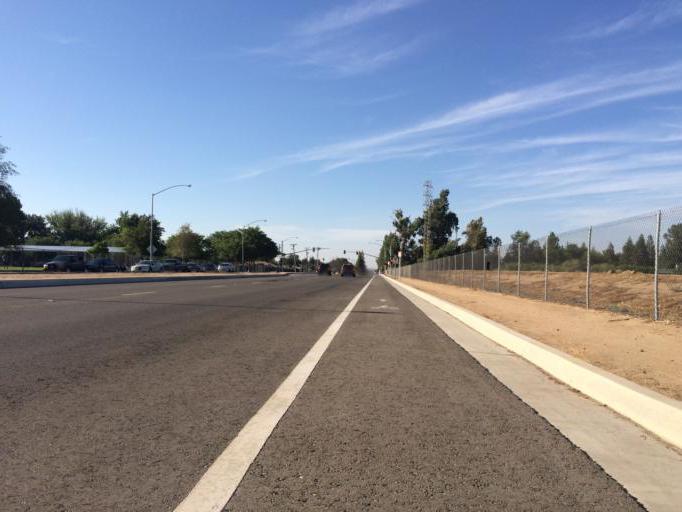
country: US
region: California
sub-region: Fresno County
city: Sunnyside
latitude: 36.7420
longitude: -119.6819
